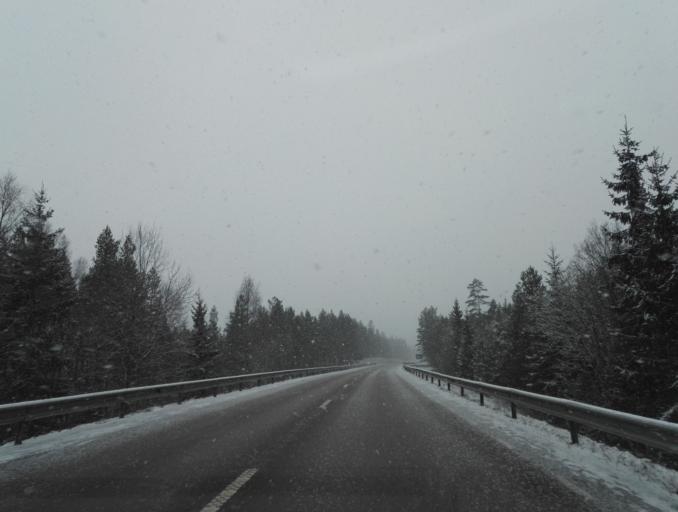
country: SE
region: Kronoberg
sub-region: Uppvidinge Kommun
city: Lenhovda
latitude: 57.0950
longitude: 15.1986
